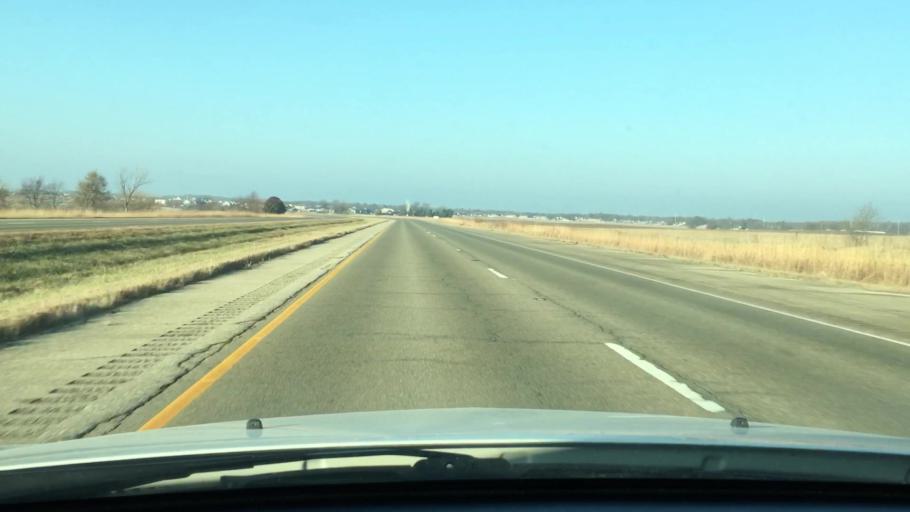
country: US
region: Illinois
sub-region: Tazewell County
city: Washington
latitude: 40.7277
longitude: -89.4170
